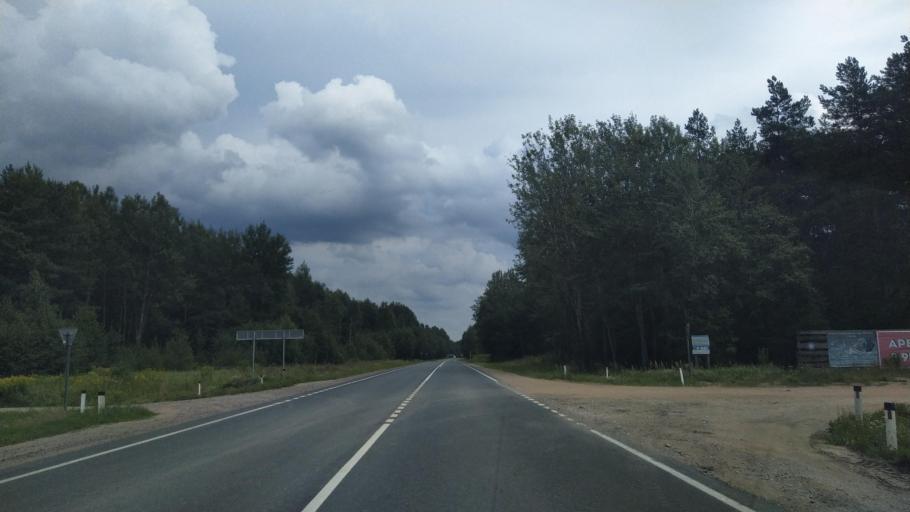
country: RU
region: Pskov
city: Pskov
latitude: 57.8335
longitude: 28.5196
